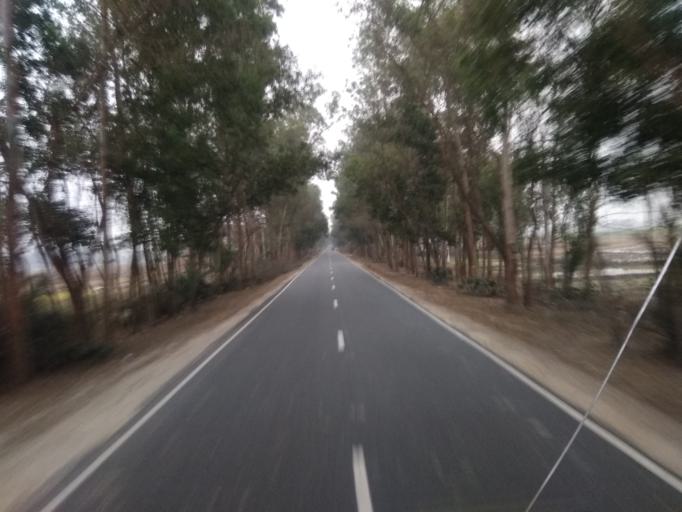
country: BD
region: Rajshahi
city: Bogra
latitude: 24.6599
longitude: 89.2669
